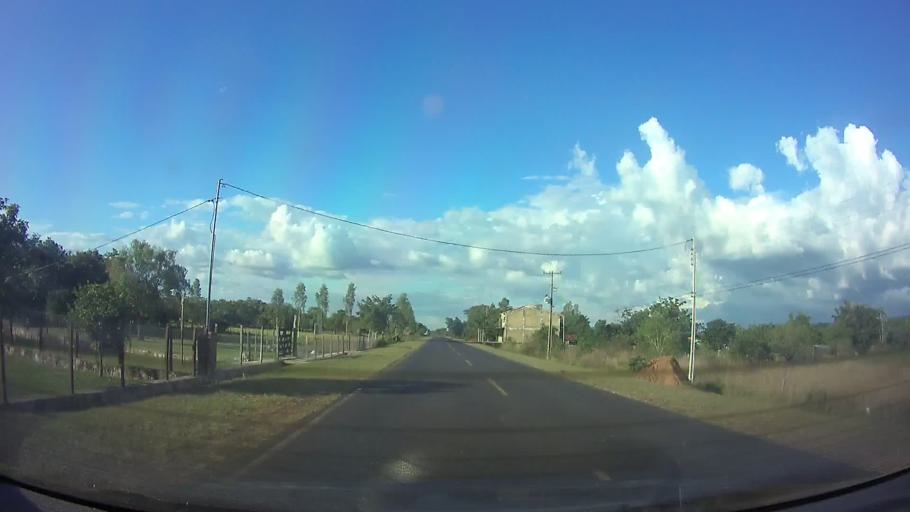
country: PY
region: Cordillera
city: Emboscada
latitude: -25.1565
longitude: -57.2624
